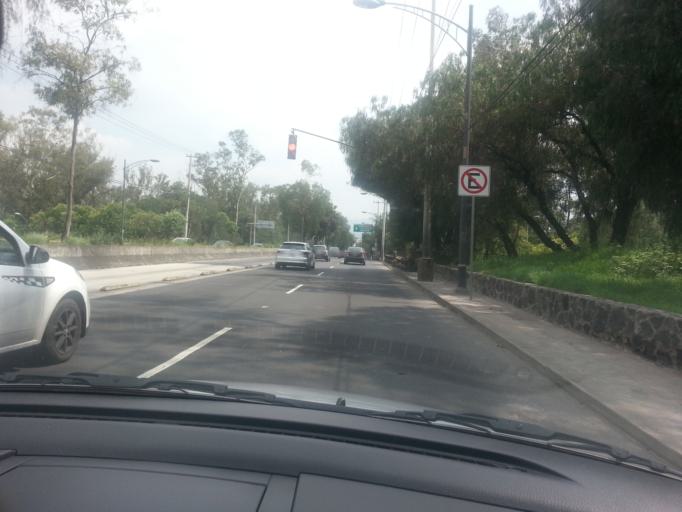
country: MX
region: Mexico City
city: Magdalena Contreras
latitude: 19.3279
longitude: -99.1891
